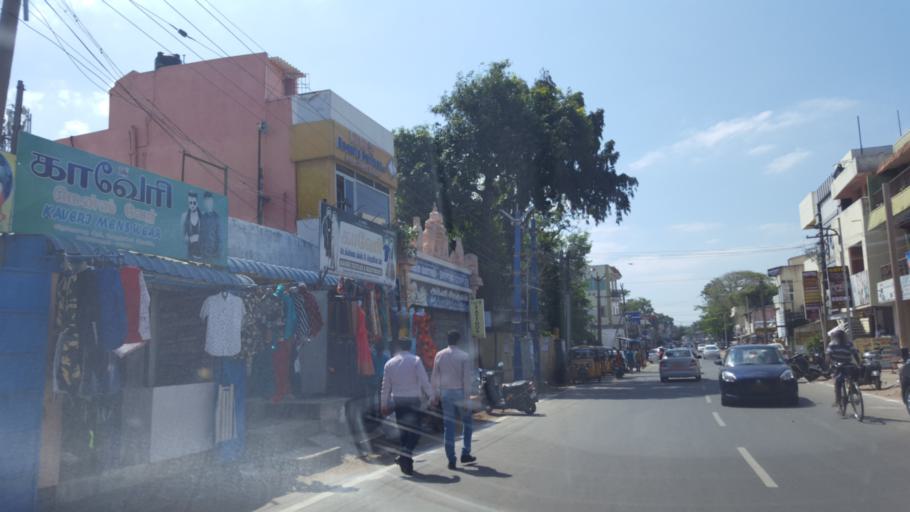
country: IN
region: Tamil Nadu
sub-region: Kancheepuram
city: Mamallapuram
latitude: 12.6207
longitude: 80.1945
